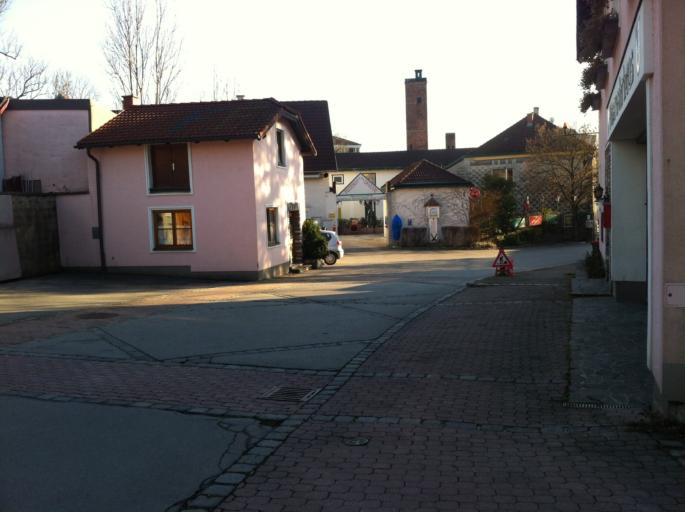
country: AT
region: Lower Austria
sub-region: Politischer Bezirk Wien-Umgebung
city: Gablitz
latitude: 48.2293
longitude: 16.1515
